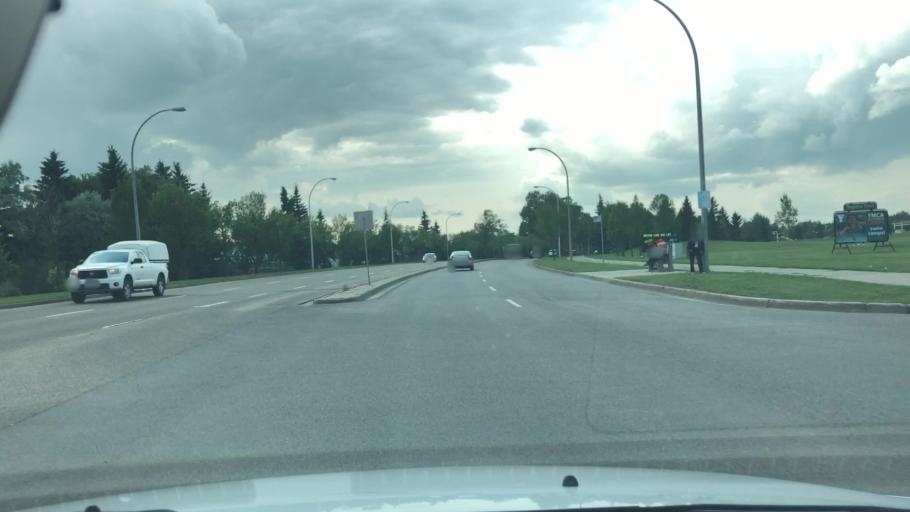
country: CA
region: Alberta
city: Edmonton
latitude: 53.6143
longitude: -113.5204
